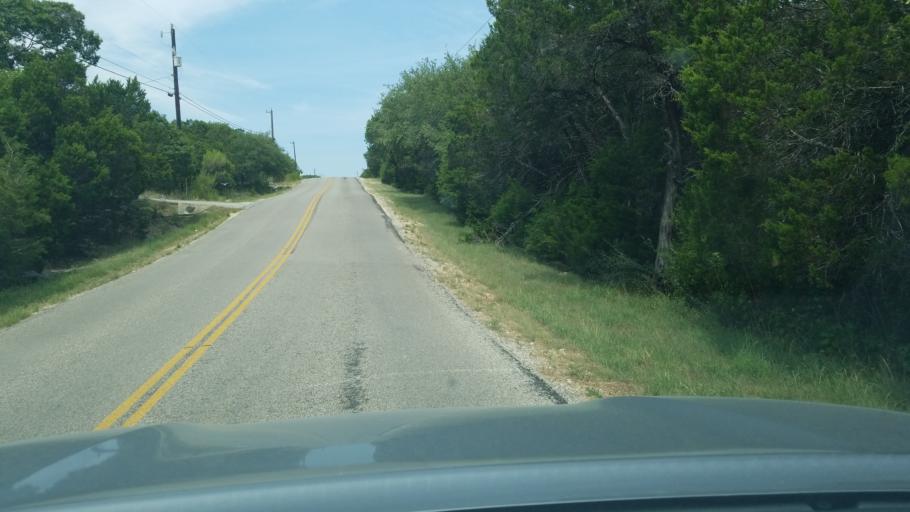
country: US
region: Texas
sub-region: Comal County
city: Bulverde
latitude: 29.7758
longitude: -98.4341
